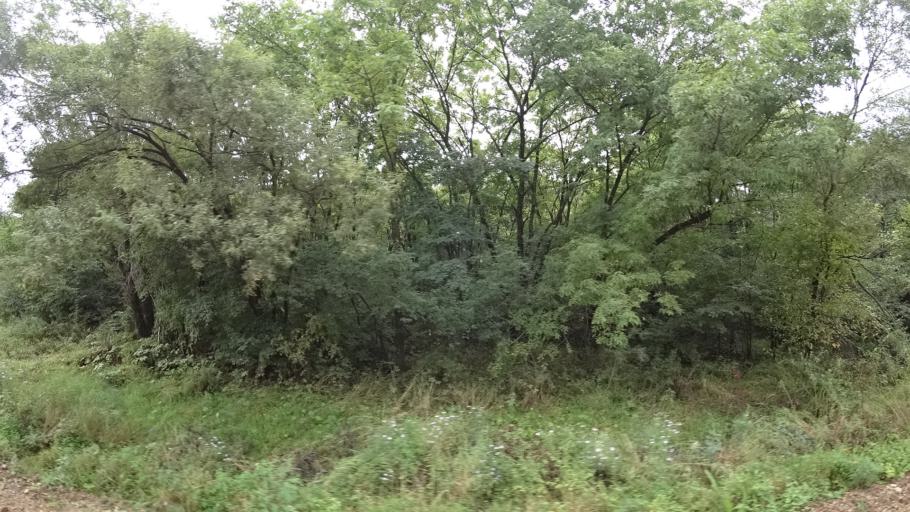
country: RU
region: Primorskiy
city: Lyalichi
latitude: 44.0809
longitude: 132.4507
